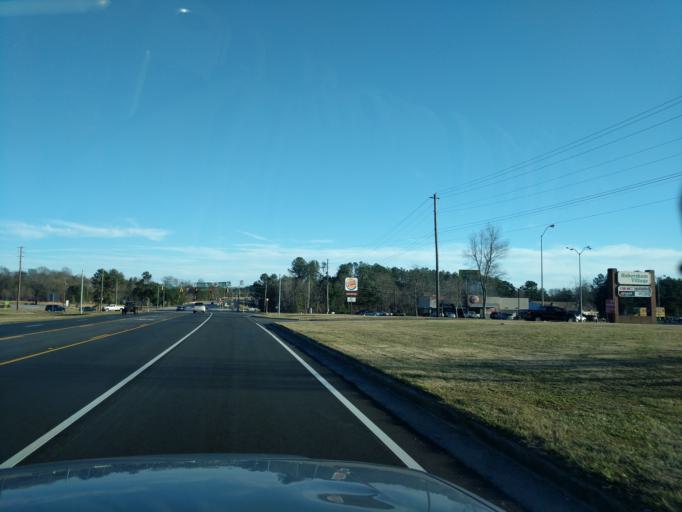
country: US
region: Georgia
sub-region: Habersham County
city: Demorest
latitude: 34.5420
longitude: -83.5426
